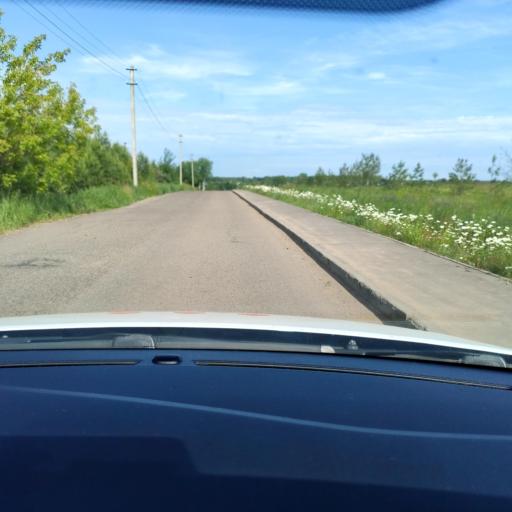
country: RU
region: Tatarstan
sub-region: Gorod Kazan'
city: Kazan
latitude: 55.8913
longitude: 49.0920
